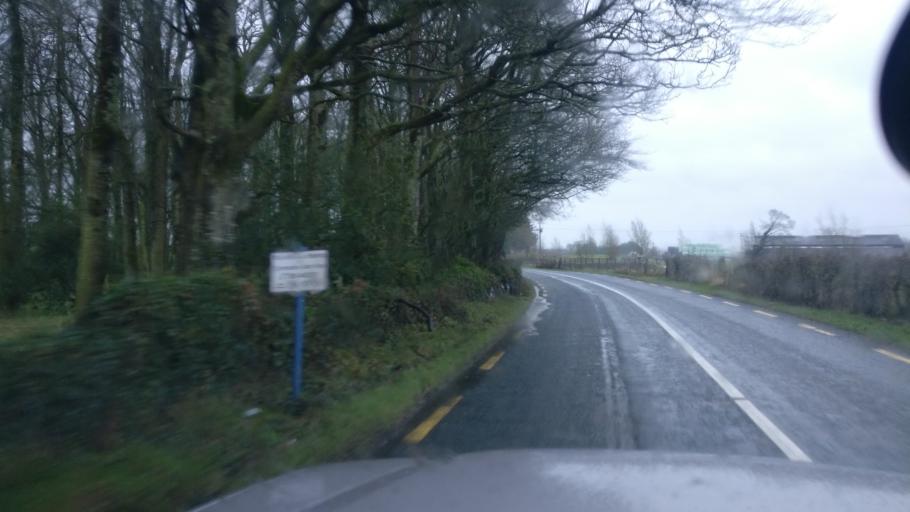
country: IE
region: Connaught
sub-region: County Galway
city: Ballinasloe
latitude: 53.2564
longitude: -8.1816
